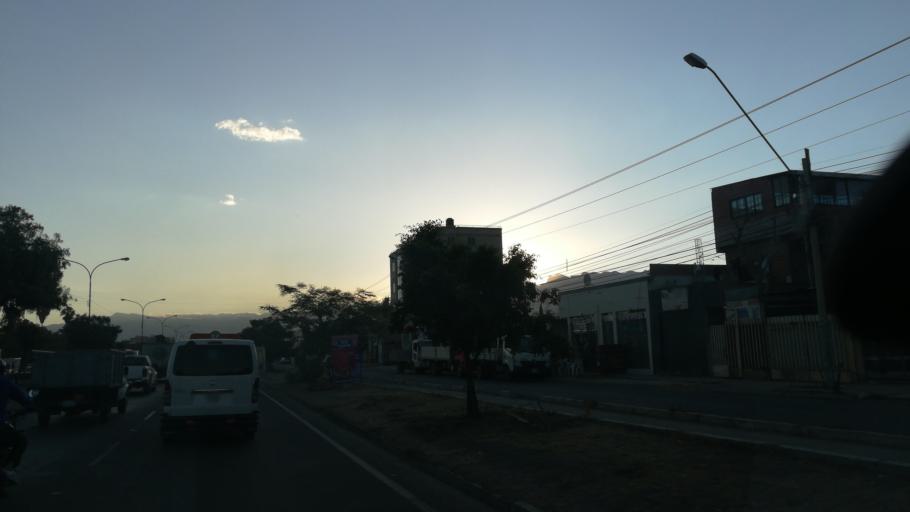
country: BO
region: Cochabamba
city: Cochabamba
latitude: -17.3925
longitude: -66.2010
